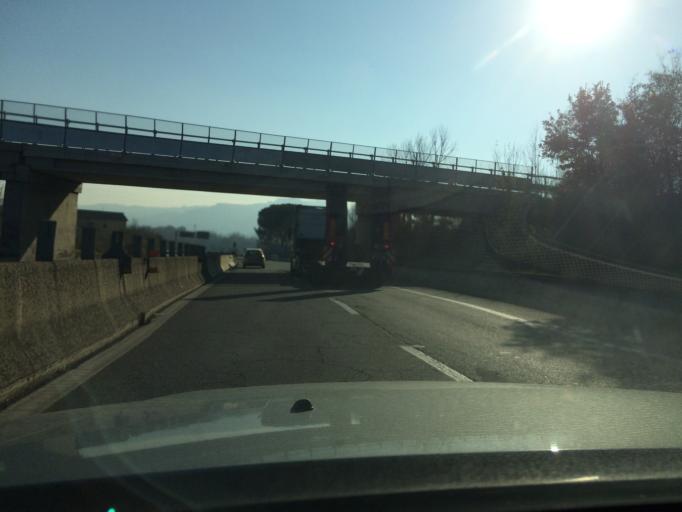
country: IT
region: Umbria
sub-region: Provincia di Perugia
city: Ponterio-Pian di Porto
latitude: 42.8213
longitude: 12.3996
